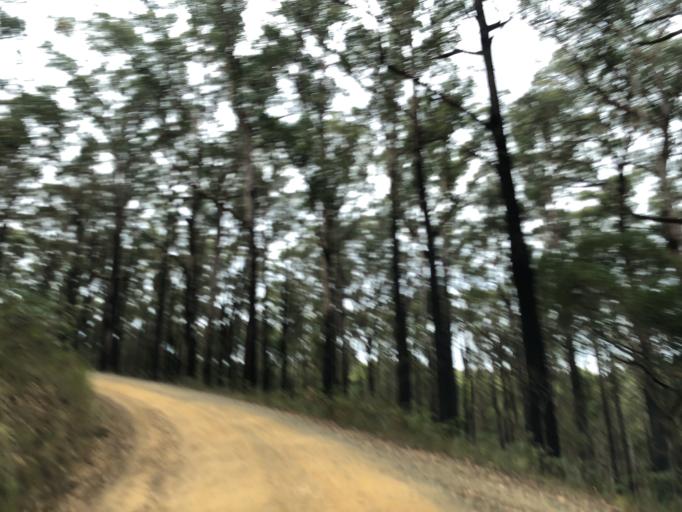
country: AU
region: Victoria
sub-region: Moorabool
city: Bacchus Marsh
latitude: -37.4691
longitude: 144.3294
